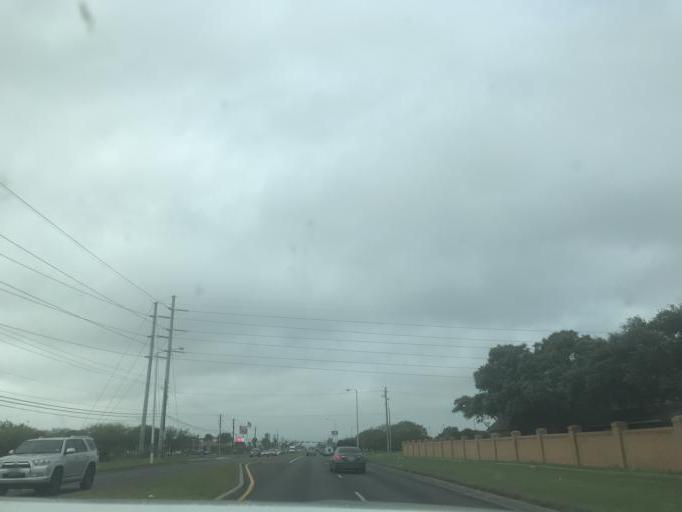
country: US
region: Texas
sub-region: Nueces County
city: Corpus Christi
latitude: 27.6815
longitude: -97.3758
